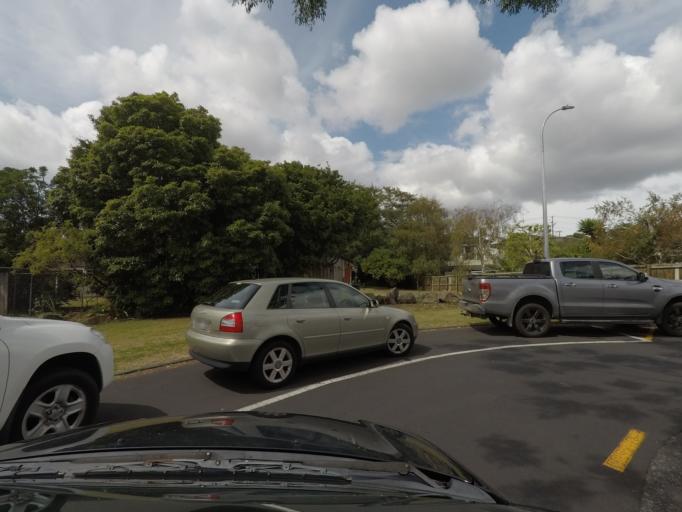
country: NZ
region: Auckland
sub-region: Auckland
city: Rosebank
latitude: -36.8822
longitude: 174.7096
